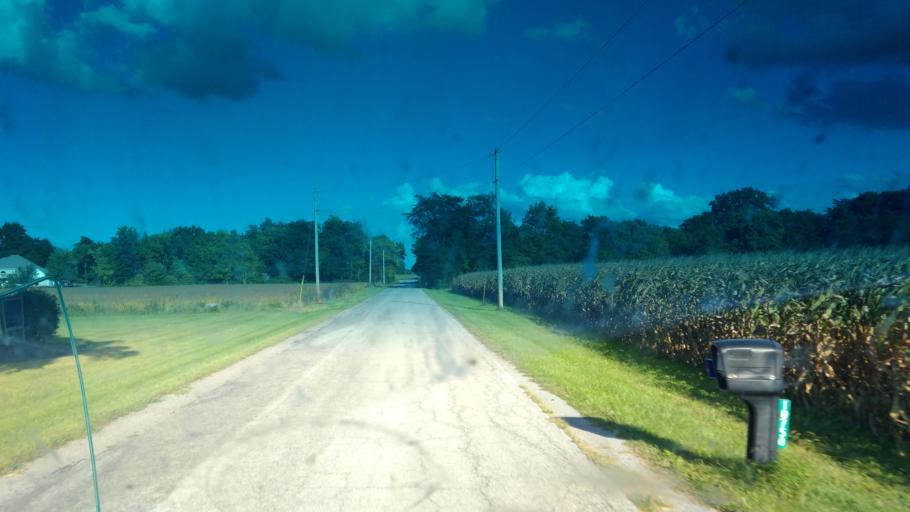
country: US
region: Ohio
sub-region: Hancock County
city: Arlington
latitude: 40.9359
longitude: -83.6736
